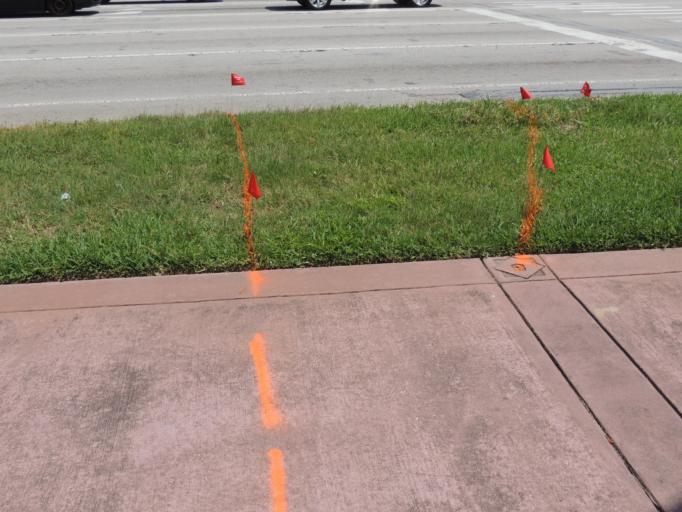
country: US
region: Florida
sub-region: Osceola County
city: Celebration
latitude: 28.3325
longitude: -81.5211
